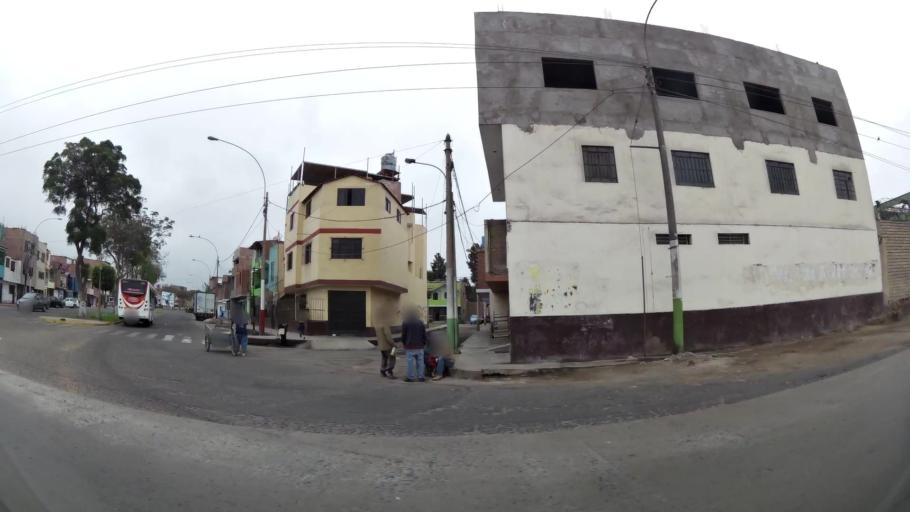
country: PE
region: Callao
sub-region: Callao
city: Callao
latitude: -12.0557
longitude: -77.1218
